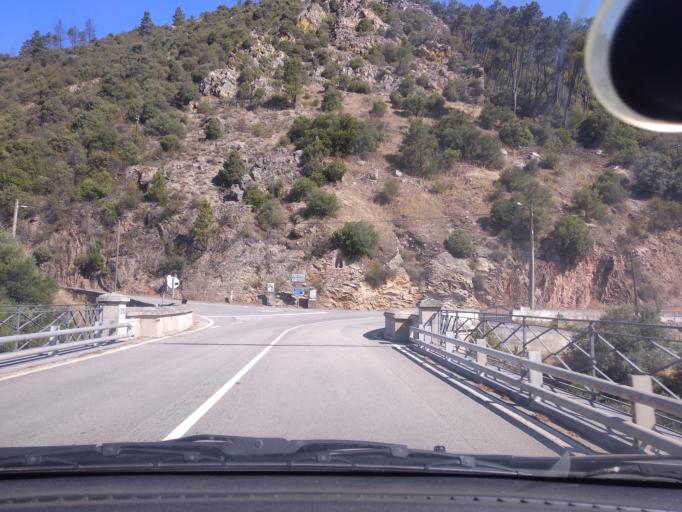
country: PT
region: Portalegre
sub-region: Nisa
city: Nisa
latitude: 39.6475
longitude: -7.6768
